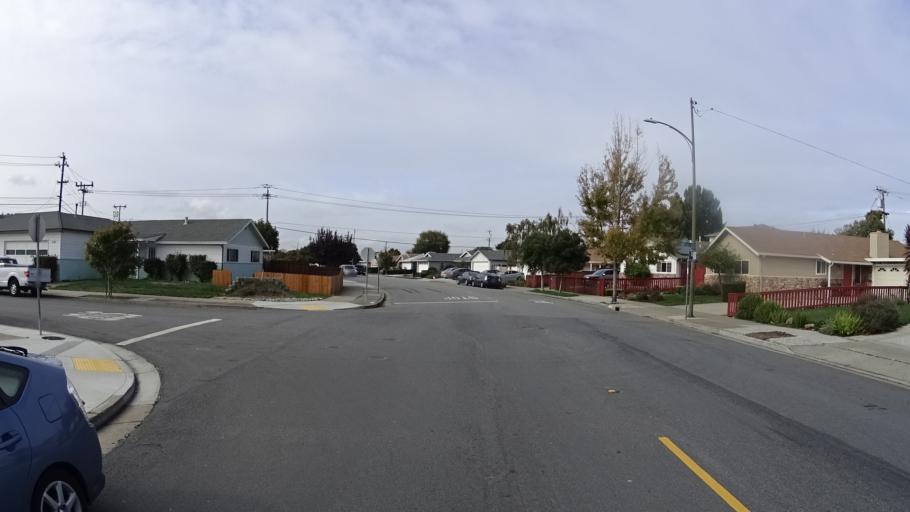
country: US
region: California
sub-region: San Mateo County
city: Belmont
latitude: 37.5268
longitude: -122.2758
